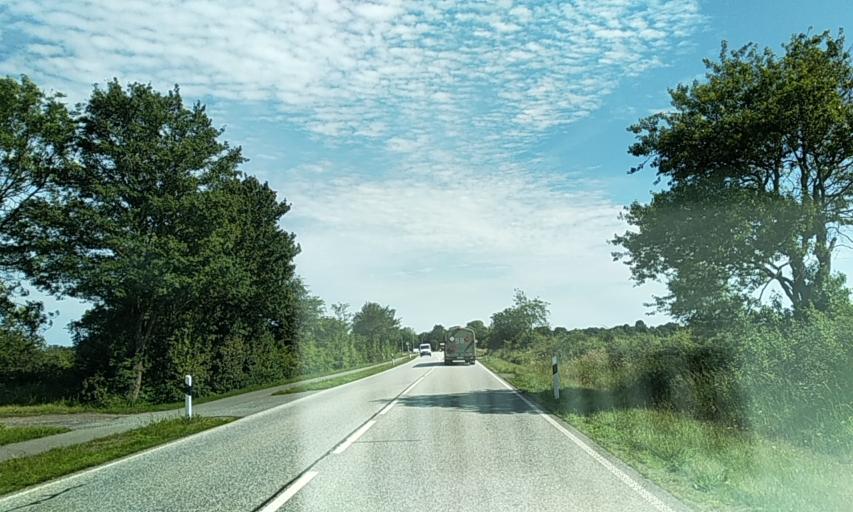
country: DE
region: Schleswig-Holstein
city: Jagel
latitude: 54.4687
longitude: 9.5423
